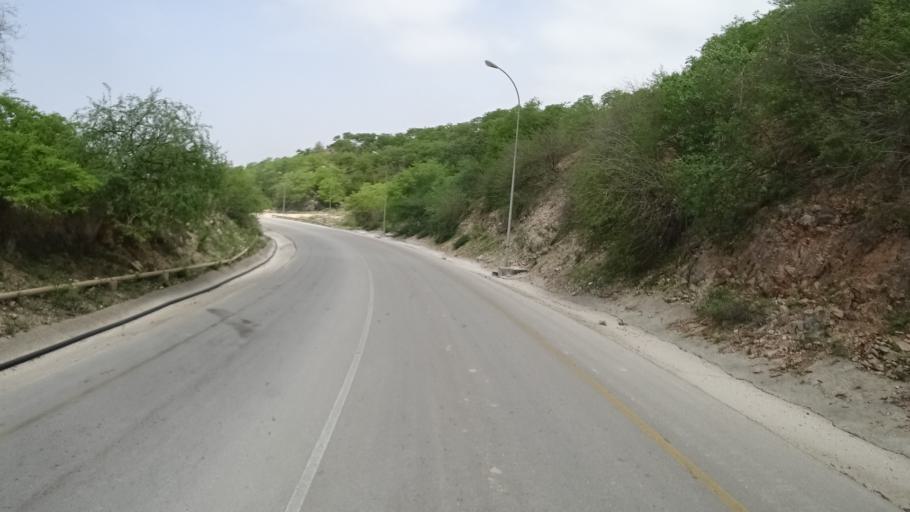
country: OM
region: Zufar
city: Salalah
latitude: 17.0730
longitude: 54.4499
